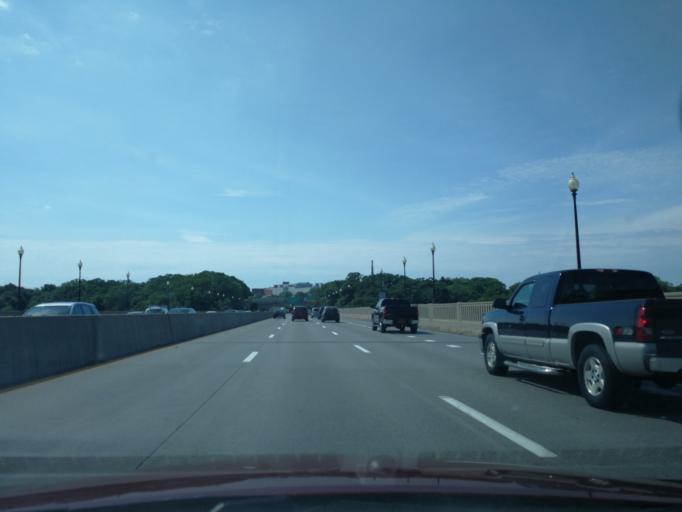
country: US
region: New York
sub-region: Monroe County
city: Rochester
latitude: 43.1922
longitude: -77.6195
